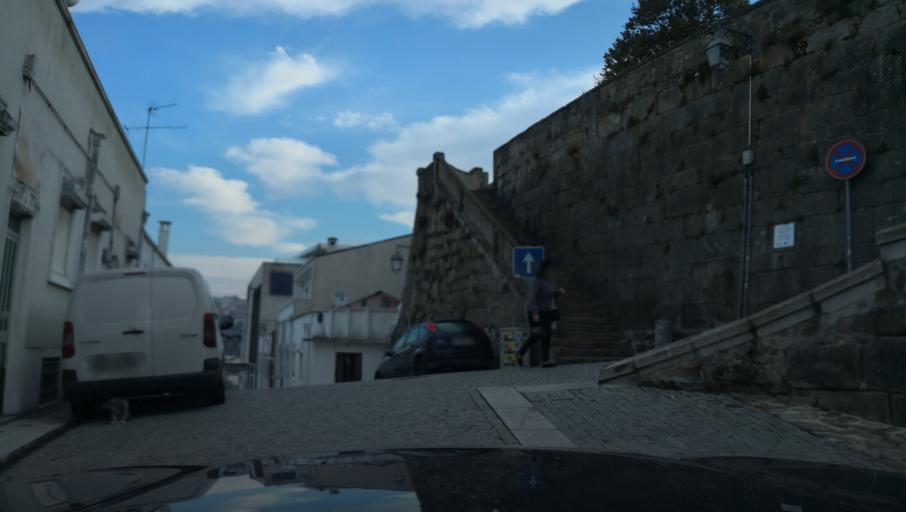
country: PT
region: Porto
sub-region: Vila Nova de Gaia
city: Vila Nova de Gaia
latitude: 41.1372
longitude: -8.6102
